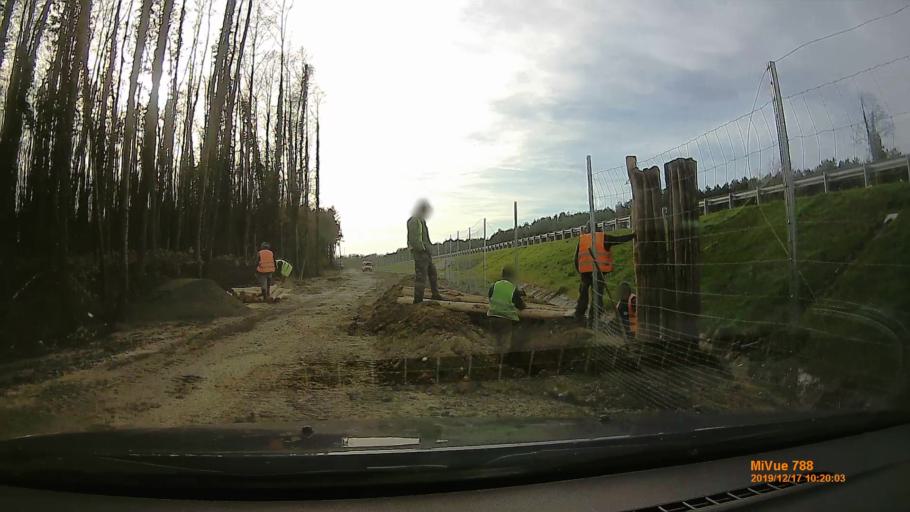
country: HU
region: Somogy
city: Karad
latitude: 46.6506
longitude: 17.7864
